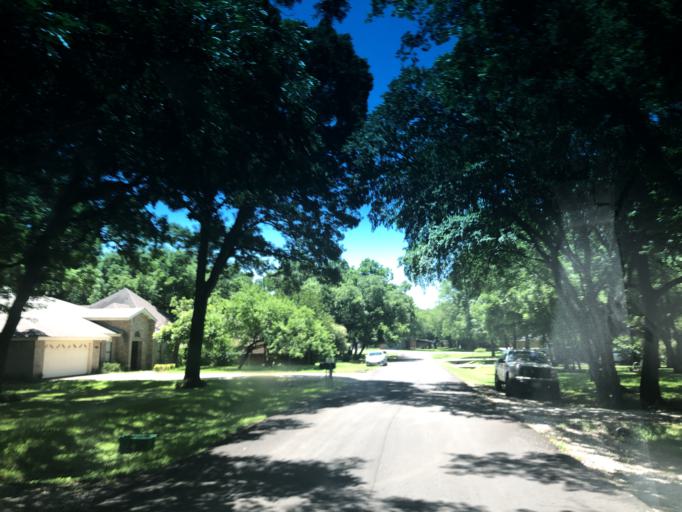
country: US
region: Texas
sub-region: Dallas County
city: Grand Prairie
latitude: 32.7750
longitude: -97.0346
